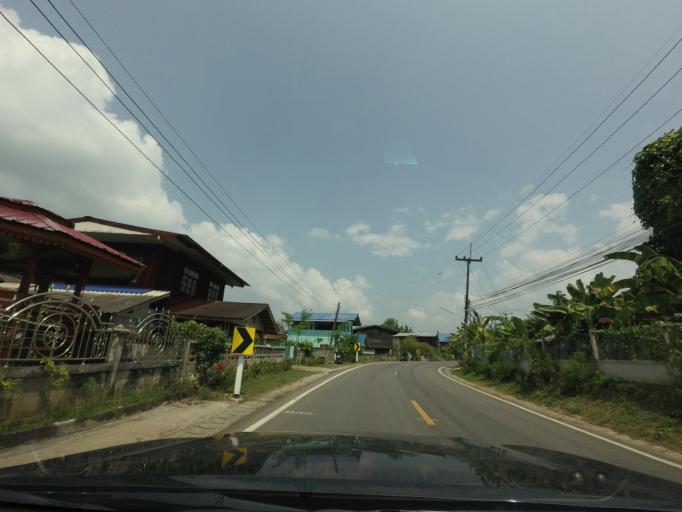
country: TH
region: Nan
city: Santi Suk
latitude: 18.9543
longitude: 100.9224
